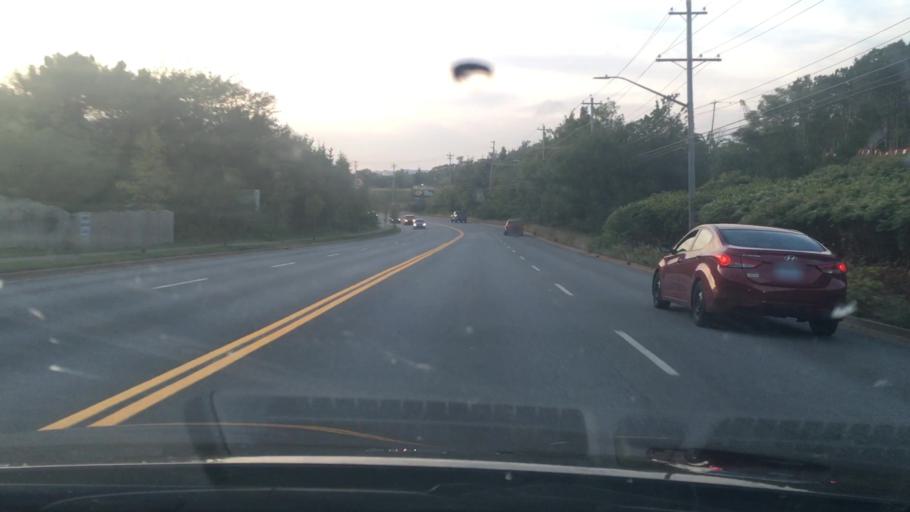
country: CA
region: Nova Scotia
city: Halifax
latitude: 44.6330
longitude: -63.5228
